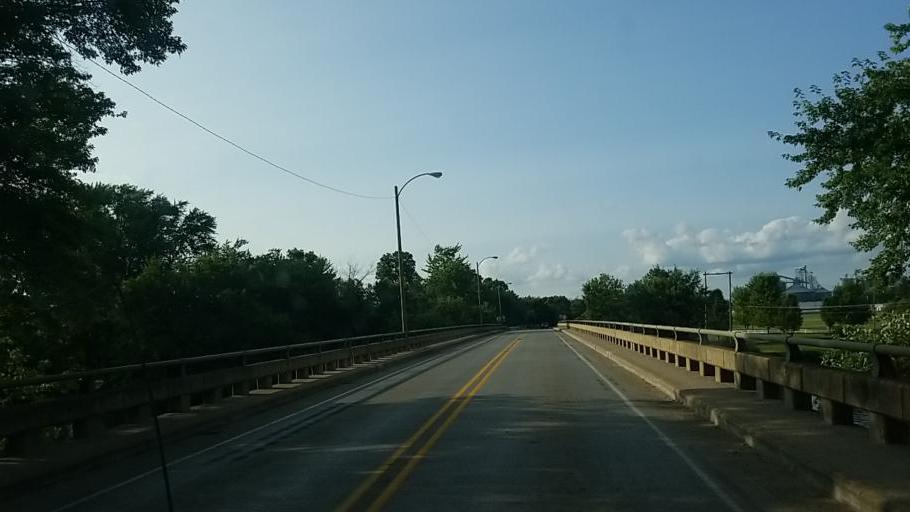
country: US
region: Michigan
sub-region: Kent County
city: Lowell
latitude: 42.9247
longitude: -85.3427
